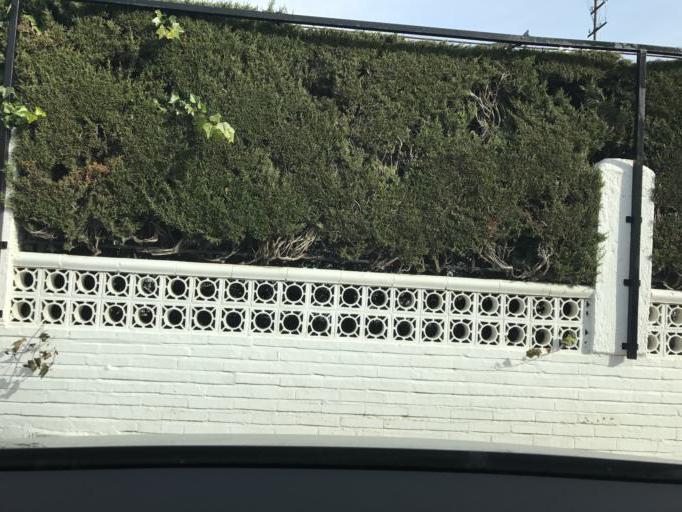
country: ES
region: Andalusia
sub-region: Provincia de Granada
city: Churriana de la Vega
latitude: 37.1395
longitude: -3.6508
